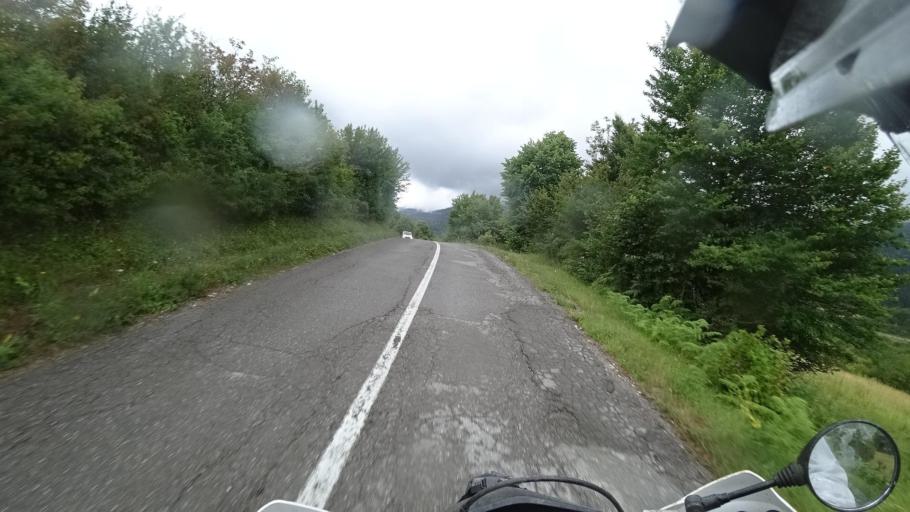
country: HR
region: Karlovacka
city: Plaski
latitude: 45.0206
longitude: 15.4129
